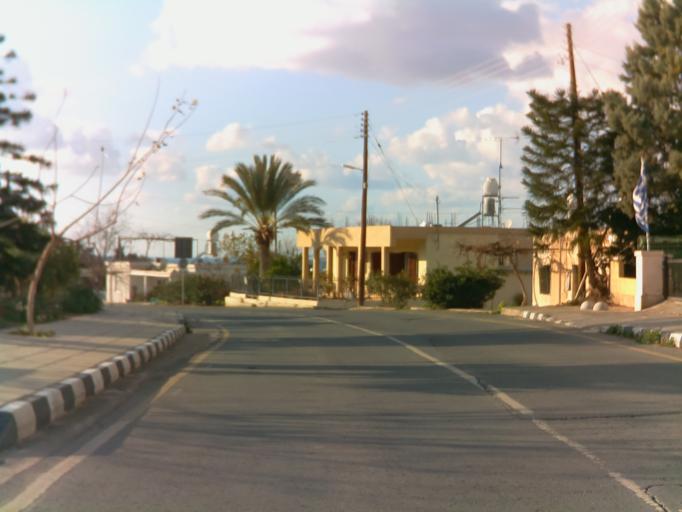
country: CY
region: Pafos
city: Kissonerga
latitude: 34.8218
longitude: 32.4057
